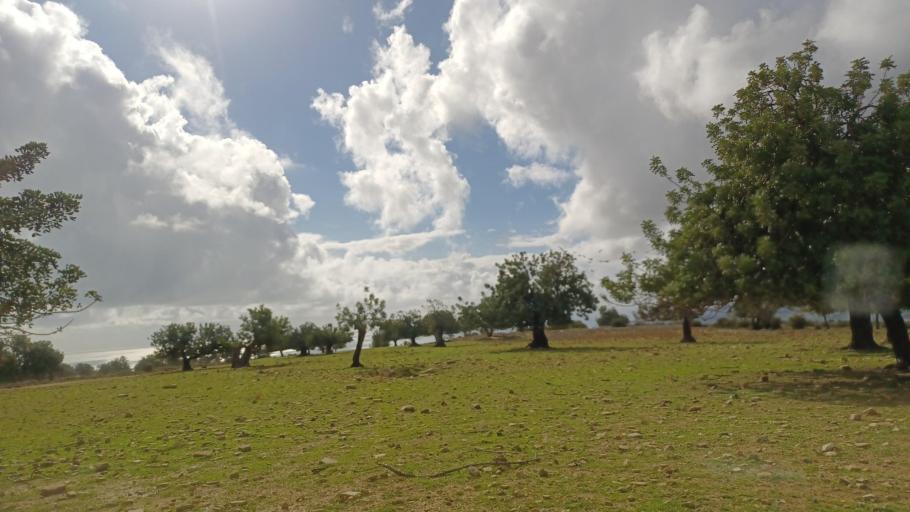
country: CY
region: Limassol
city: Sotira
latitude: 34.7244
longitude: 32.8260
